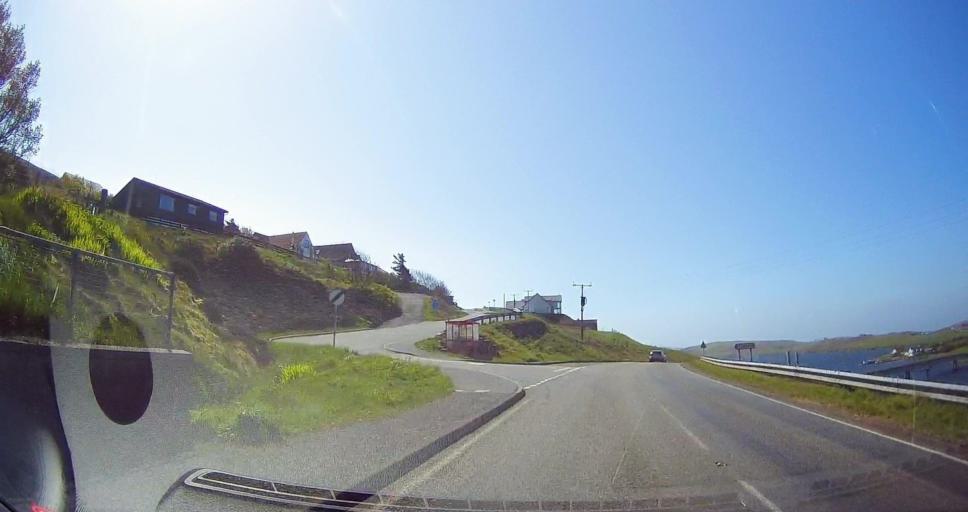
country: GB
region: Scotland
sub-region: Shetland Islands
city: Lerwick
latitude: 60.1315
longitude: -1.2674
